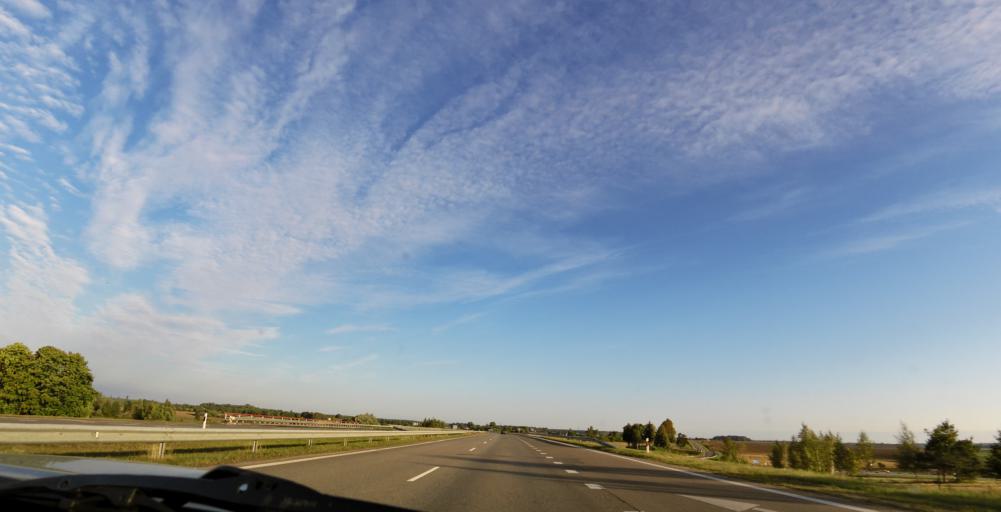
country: LT
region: Vilnius County
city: Ukmerge
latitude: 55.3014
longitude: 24.7953
